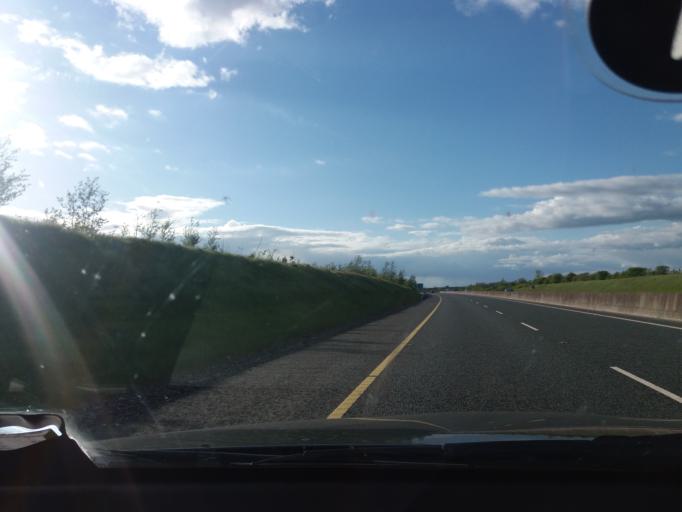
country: IE
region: Leinster
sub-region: Kildare
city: Castledermot
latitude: 52.8785
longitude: -6.8443
